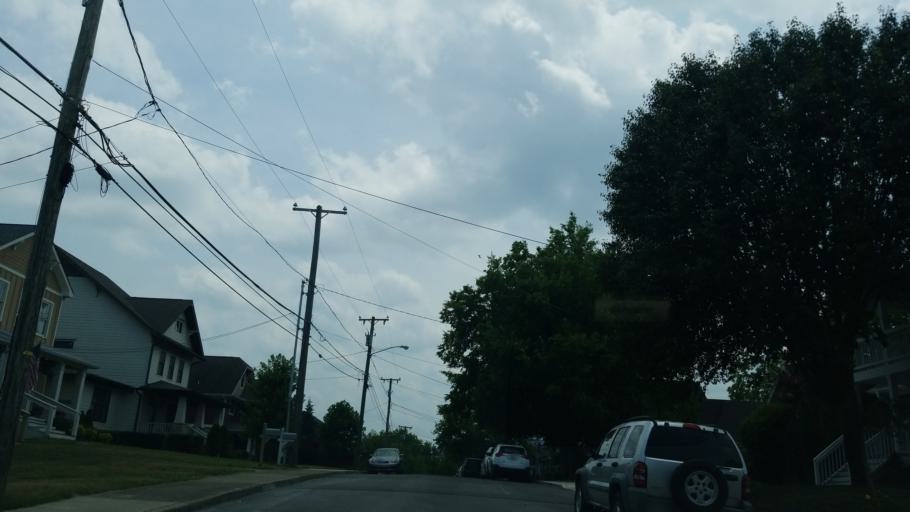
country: US
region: Tennessee
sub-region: Davidson County
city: Nashville
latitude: 36.1702
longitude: -86.7946
